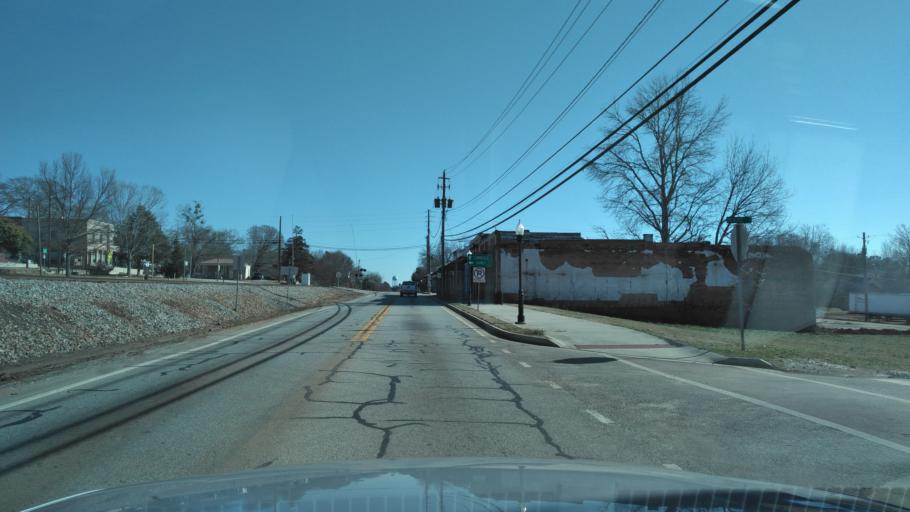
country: US
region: Georgia
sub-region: Banks County
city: Maysville
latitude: 34.2537
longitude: -83.5624
